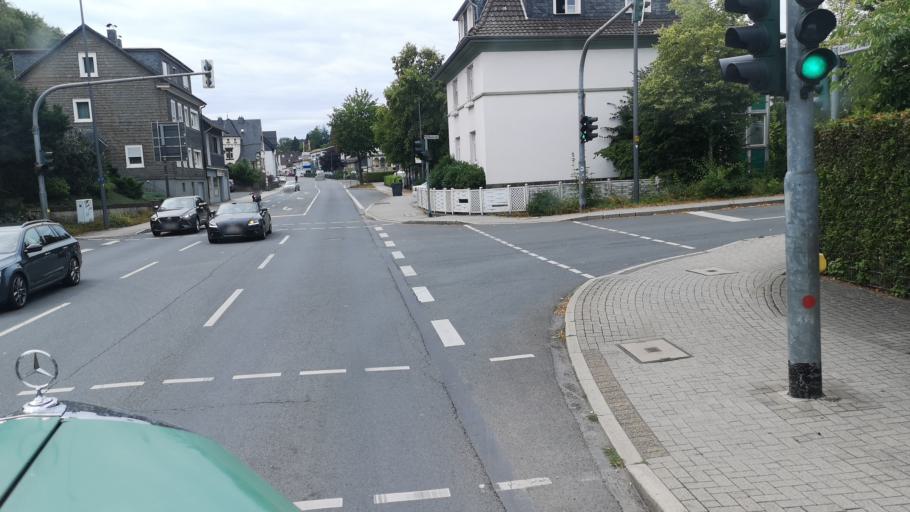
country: DE
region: North Rhine-Westphalia
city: Wipperfurth
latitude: 51.1153
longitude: 7.3905
